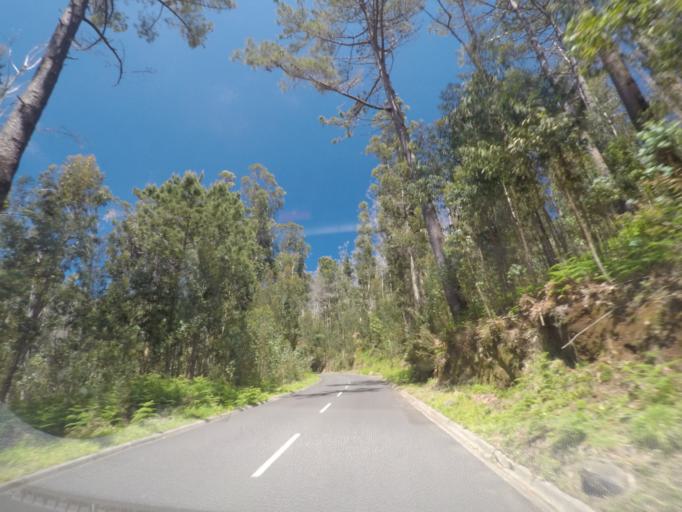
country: PT
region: Madeira
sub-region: Calheta
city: Arco da Calheta
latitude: 32.7342
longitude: -17.1301
